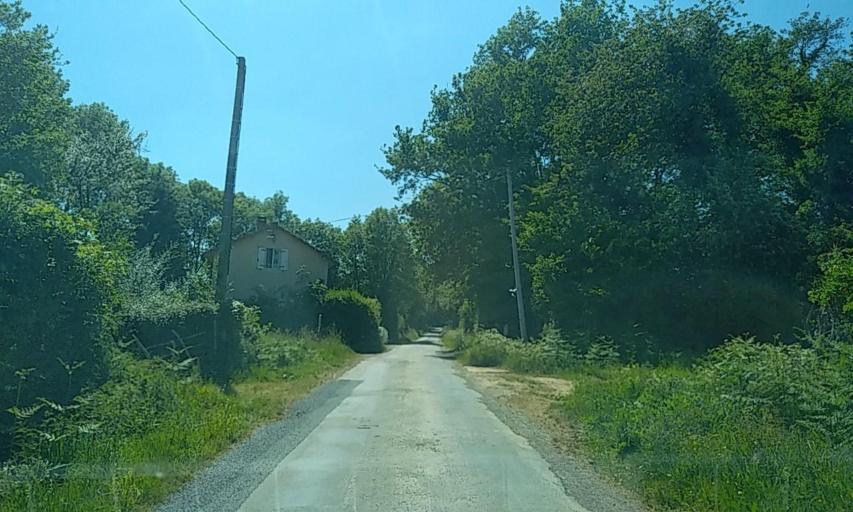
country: FR
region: Poitou-Charentes
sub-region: Departement des Deux-Sevres
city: La Chapelle-Saint-Laurent
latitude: 46.7796
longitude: -0.4813
